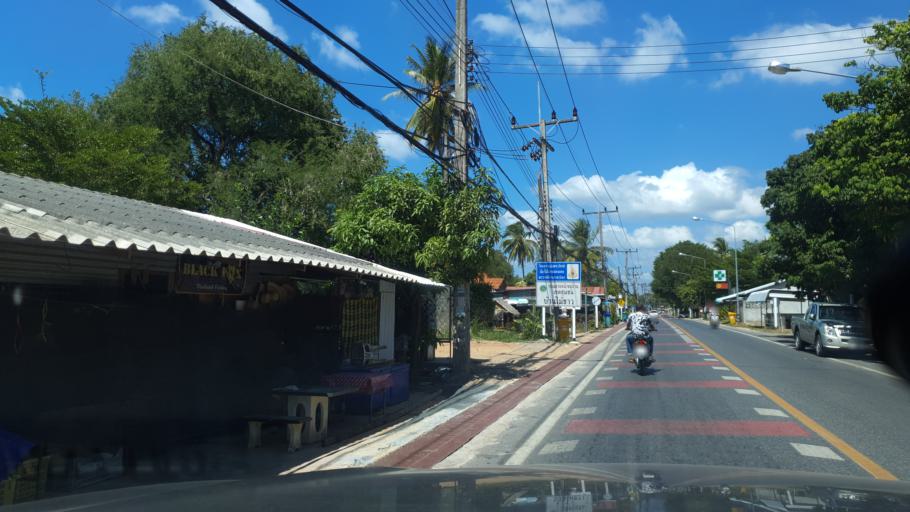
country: TH
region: Phuket
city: Thalang
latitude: 8.1222
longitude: 98.3083
